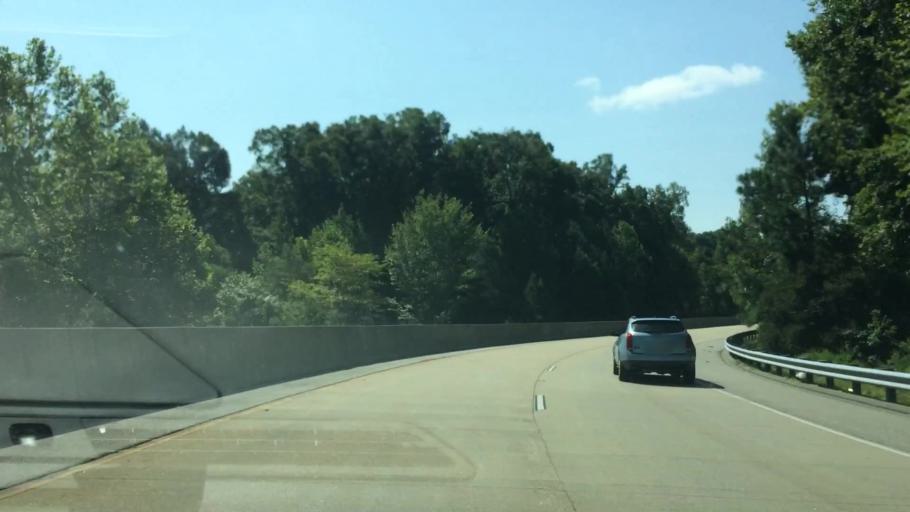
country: US
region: Virginia
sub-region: City of Williamsburg
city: Williamsburg
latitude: 37.2477
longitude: -76.6345
